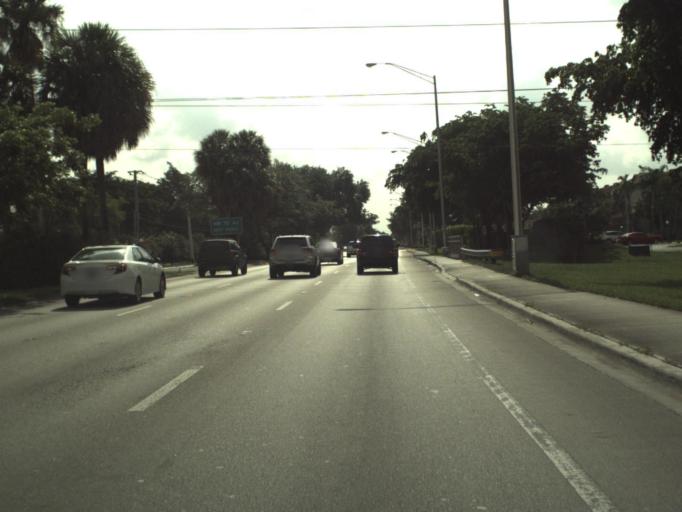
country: US
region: Florida
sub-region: Broward County
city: Plantation
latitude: 26.1485
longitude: -80.2517
